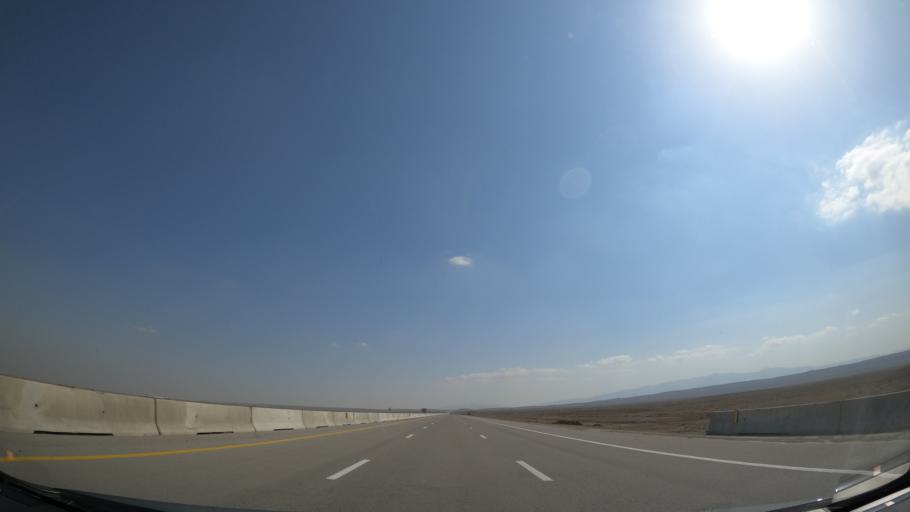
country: IR
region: Alborz
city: Nazarabad
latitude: 35.8294
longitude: 50.5020
